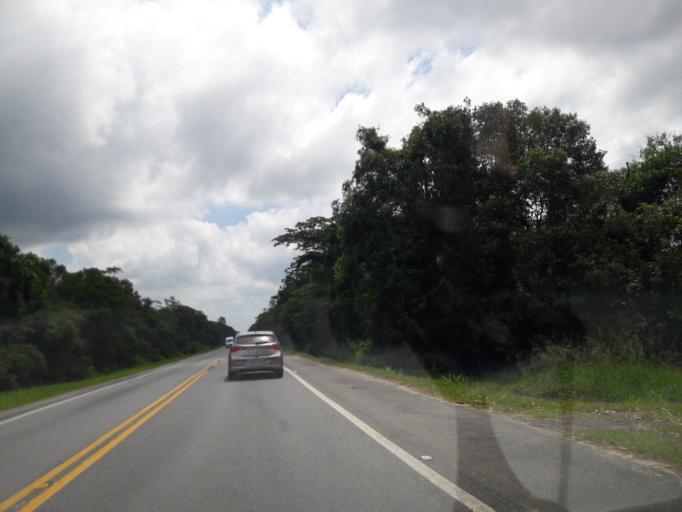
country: BR
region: Parana
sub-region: Pontal Do Parana
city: Pontal do Parana
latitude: -25.6640
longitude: -48.5191
